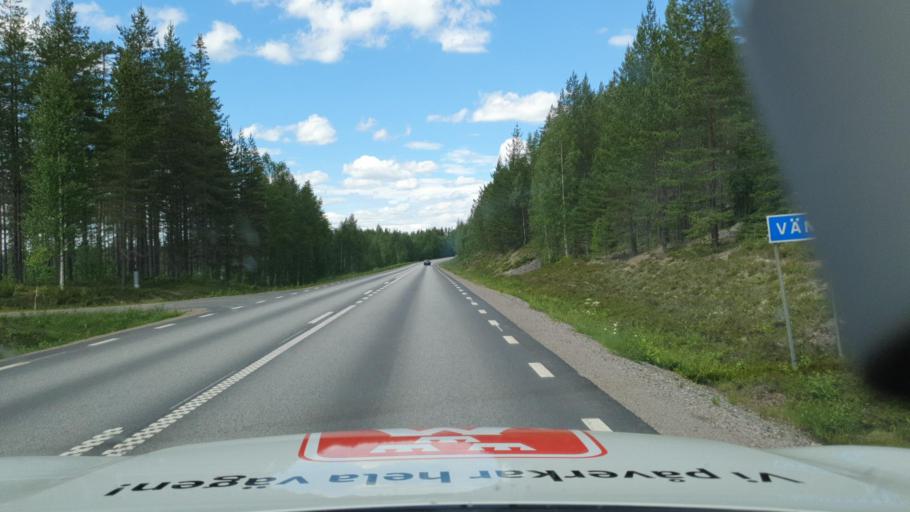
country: SE
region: Vaesterbotten
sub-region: Skelleftea Kommun
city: Langsele
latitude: 64.9674
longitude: 20.2425
